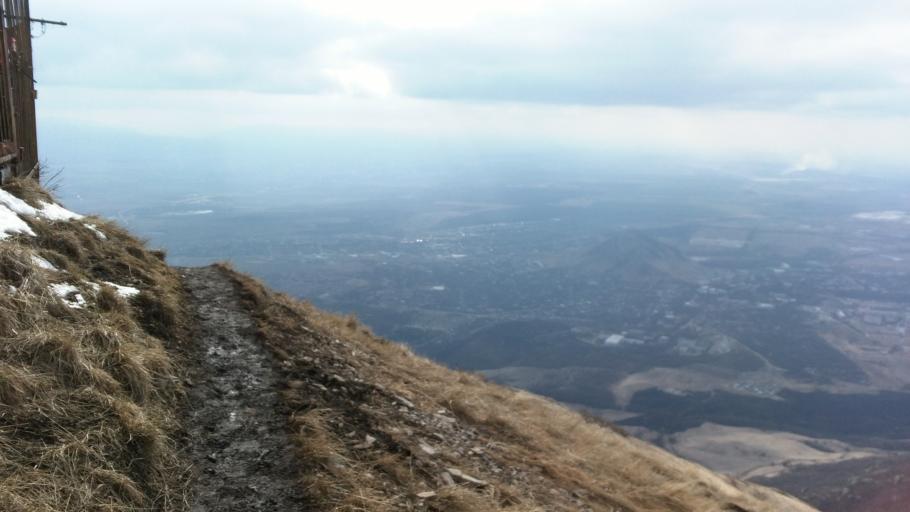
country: RU
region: Stavropol'skiy
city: Zheleznovodsk
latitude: 44.0982
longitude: 43.0220
